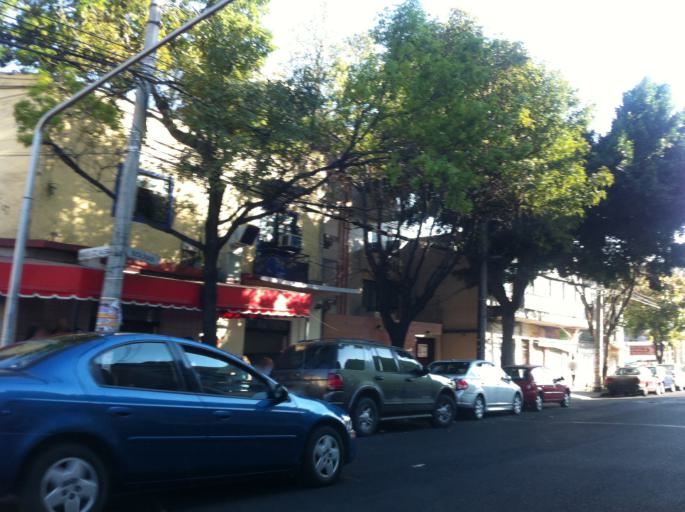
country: MX
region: Mexico City
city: Mexico City
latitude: 19.4156
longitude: -99.1410
